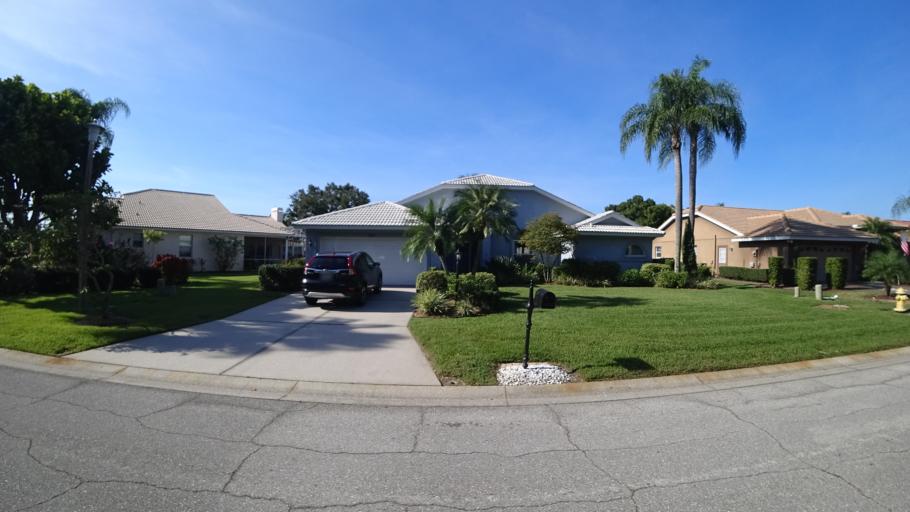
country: US
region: Florida
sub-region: Sarasota County
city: Desoto Lakes
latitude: 27.4388
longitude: -82.4799
